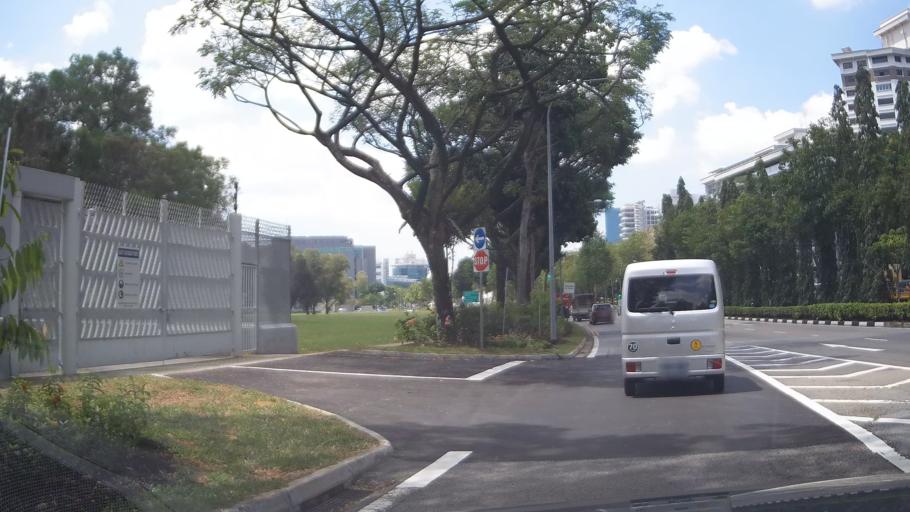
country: SG
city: Singapore
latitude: 1.3396
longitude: 103.7479
